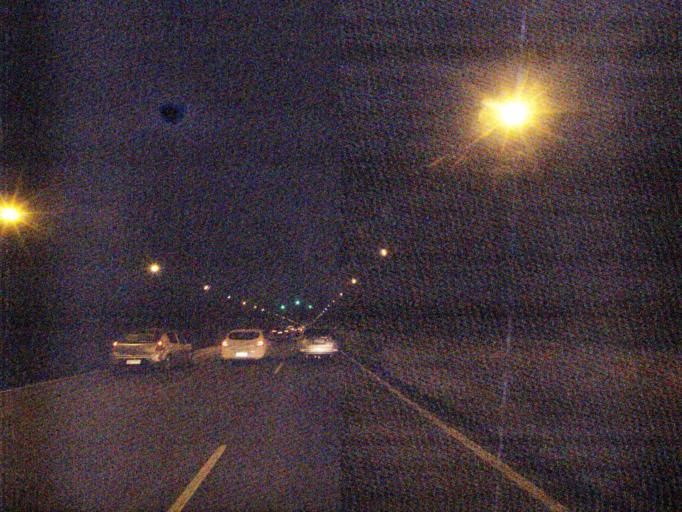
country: BR
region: Rio de Janeiro
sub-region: Rio De Janeiro
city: Rio de Janeiro
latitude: -22.9542
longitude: -43.2052
